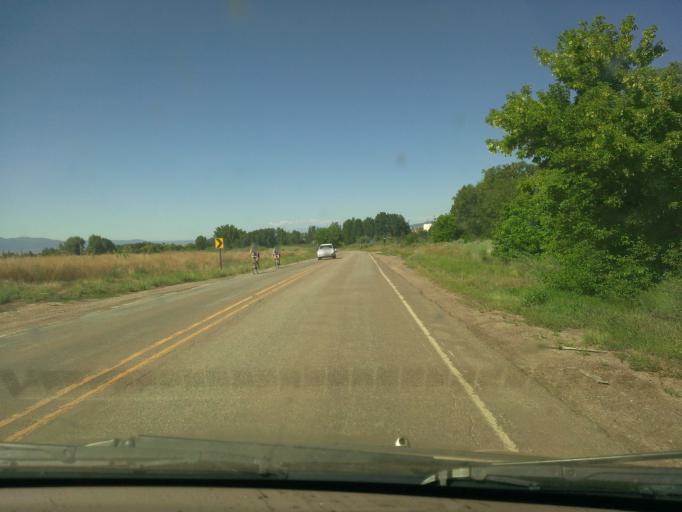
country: US
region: New Mexico
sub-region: Taos County
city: Arroyo Seco
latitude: 36.5009
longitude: -105.5906
